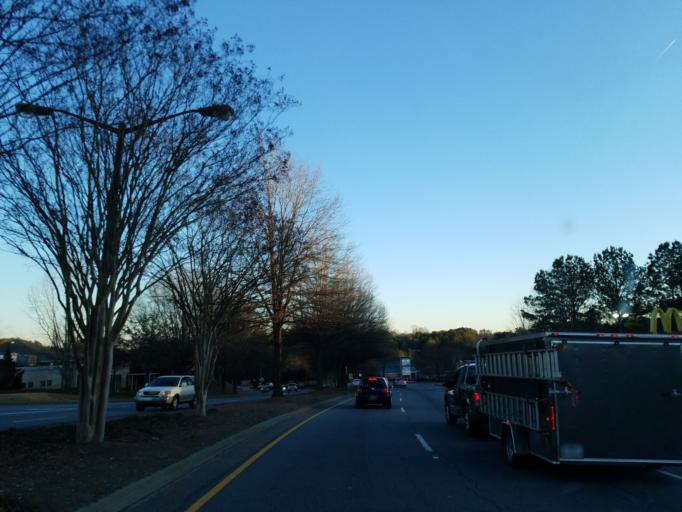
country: US
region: Georgia
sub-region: Cherokee County
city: Woodstock
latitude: 34.1100
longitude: -84.5528
